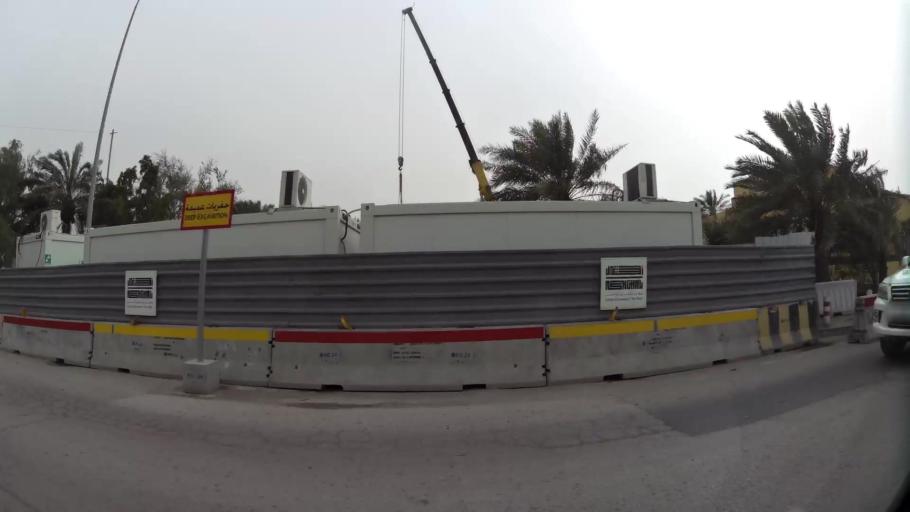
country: QA
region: Baladiyat ad Dawhah
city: Doha
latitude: 25.2484
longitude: 51.5008
